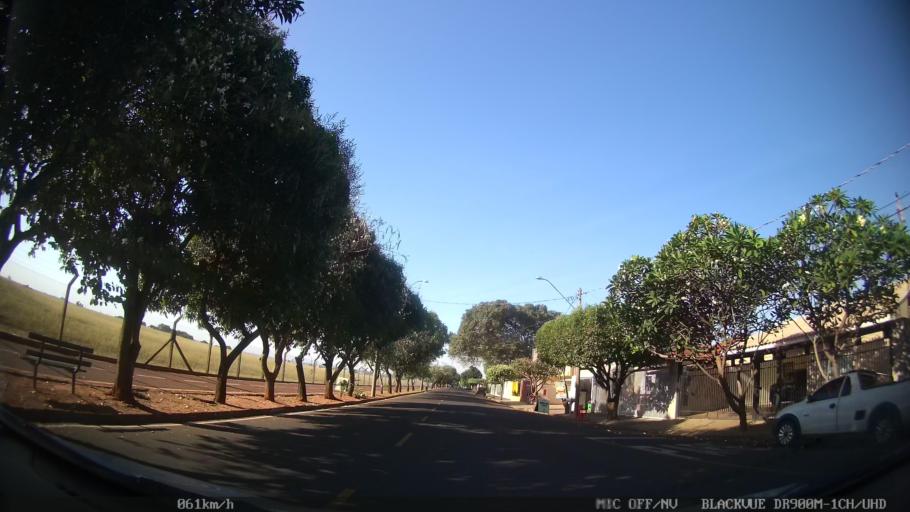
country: BR
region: Sao Paulo
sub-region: Sao Jose Do Rio Preto
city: Sao Jose do Rio Preto
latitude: -20.8188
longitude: -49.4071
